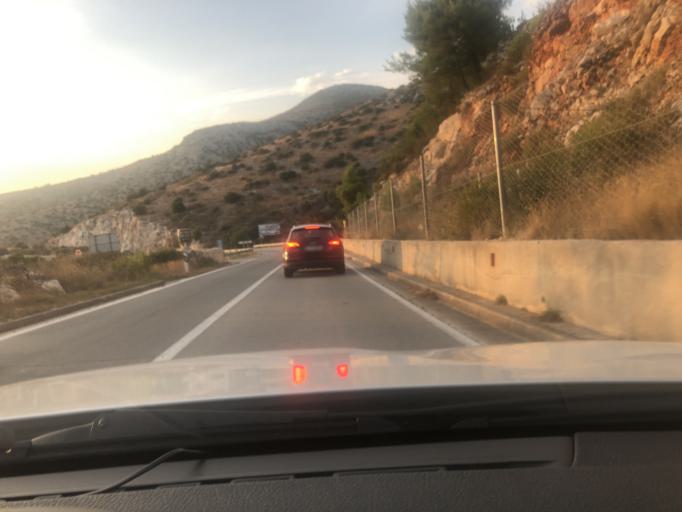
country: HR
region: Splitsko-Dalmatinska
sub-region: Grad Hvar
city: Hvar
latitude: 43.1543
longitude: 16.5103
